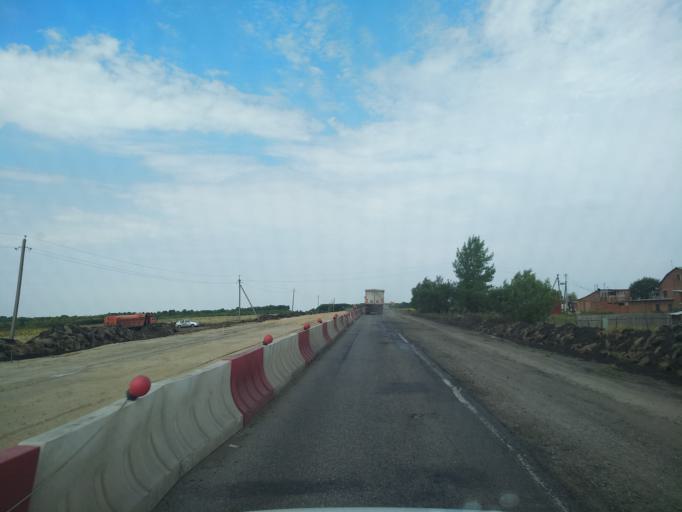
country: RU
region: Voronezj
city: Verkhnyaya Khava
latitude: 51.6768
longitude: 39.8067
